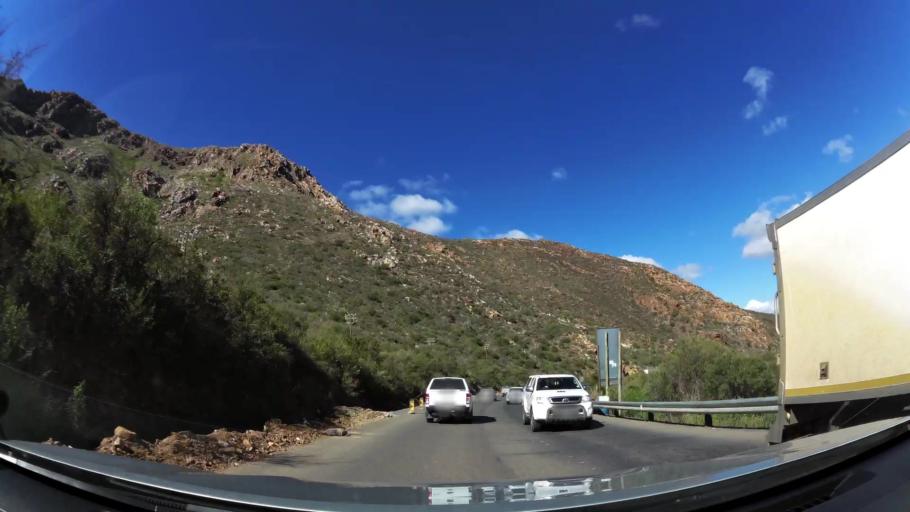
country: ZA
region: Western Cape
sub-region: Cape Winelands District Municipality
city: Ashton
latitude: -33.8195
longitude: 20.0912
